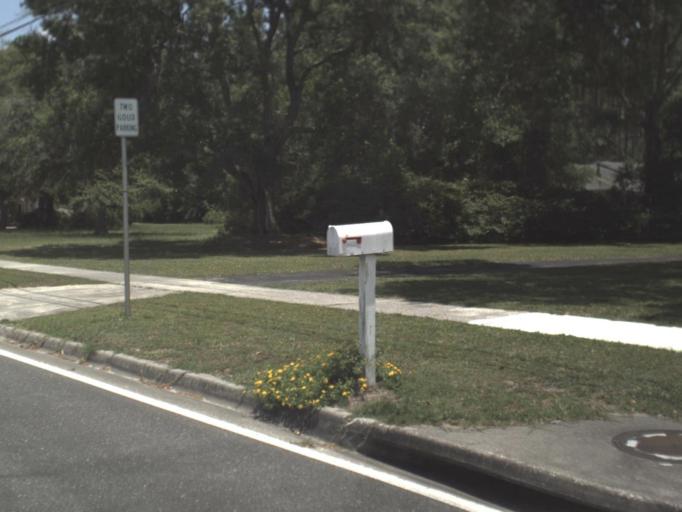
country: US
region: Florida
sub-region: Bradford County
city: Starke
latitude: 29.9597
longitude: -82.1165
